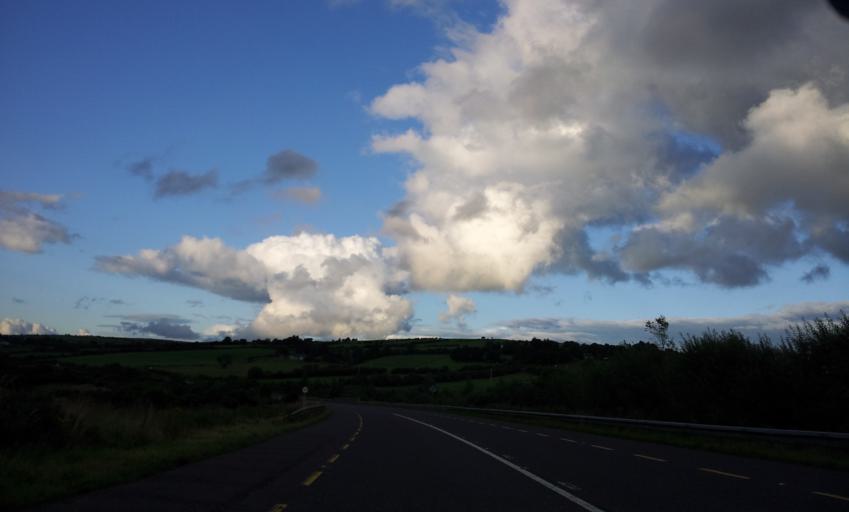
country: IE
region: Munster
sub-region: County Limerick
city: Abbeyfeale
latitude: 52.3116
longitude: -9.3653
